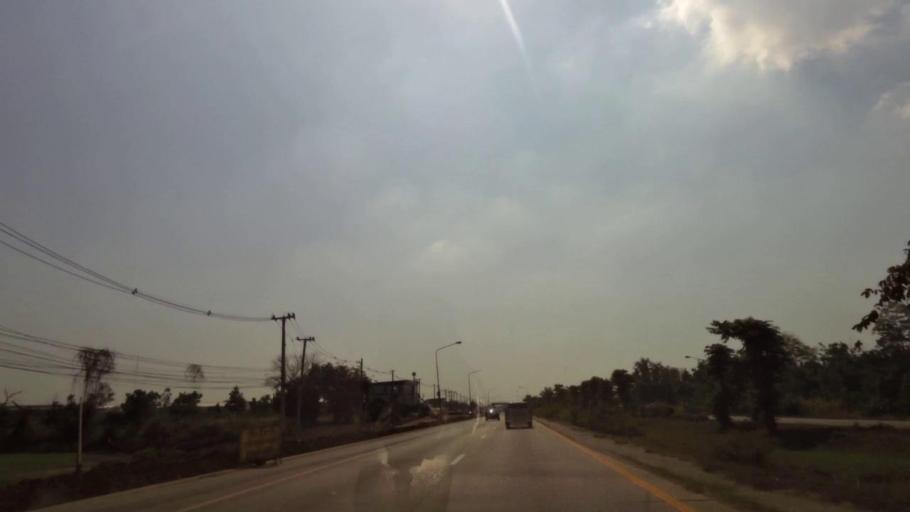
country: TH
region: Phichit
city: Wachira Barami
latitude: 16.5286
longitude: 100.1433
